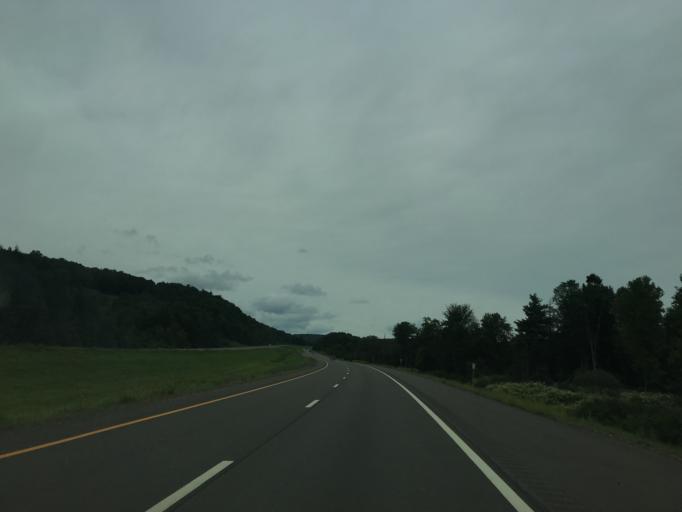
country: US
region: New York
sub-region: Broome County
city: Chenango Bridge
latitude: 42.1679
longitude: -75.7597
